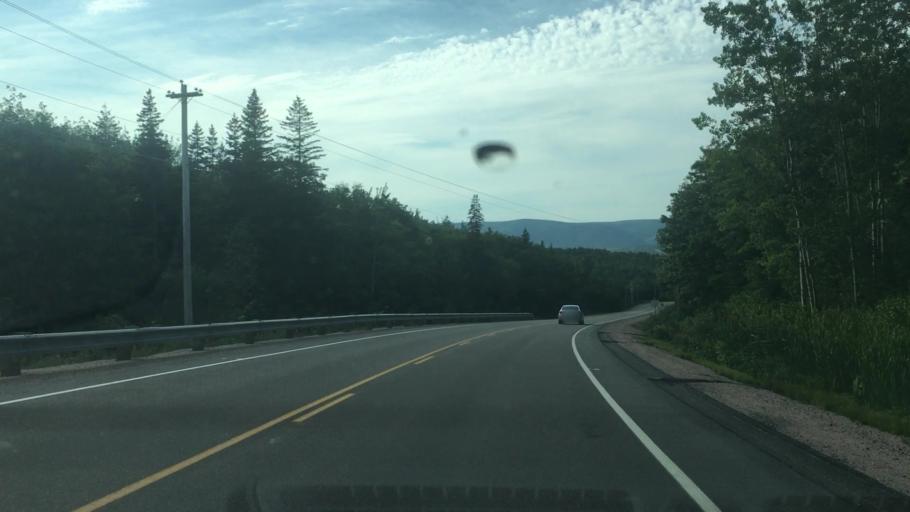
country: CA
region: Nova Scotia
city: Sydney Mines
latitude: 46.8557
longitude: -60.4572
